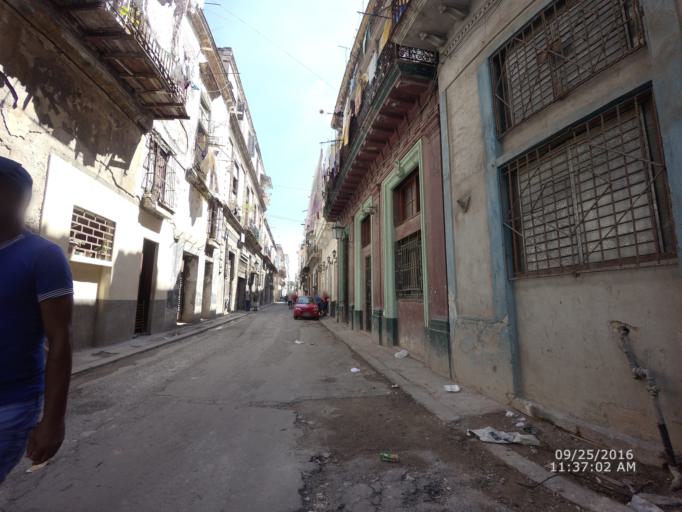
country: CU
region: La Habana
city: La Habana Vieja
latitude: 23.1371
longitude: -82.3539
